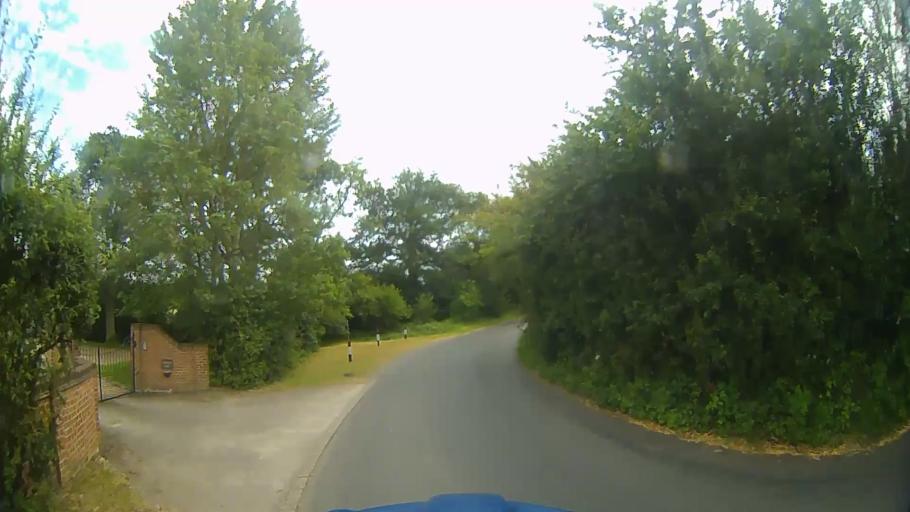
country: GB
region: England
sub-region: Hampshire
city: Basingstoke
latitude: 51.3102
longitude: -1.0666
